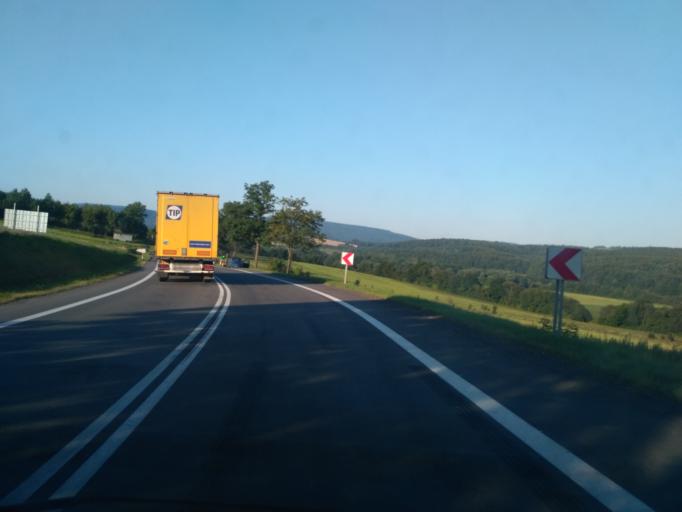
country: PL
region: Subcarpathian Voivodeship
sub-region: Powiat krosnienski
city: Dukla
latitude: 49.5867
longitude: 21.7063
